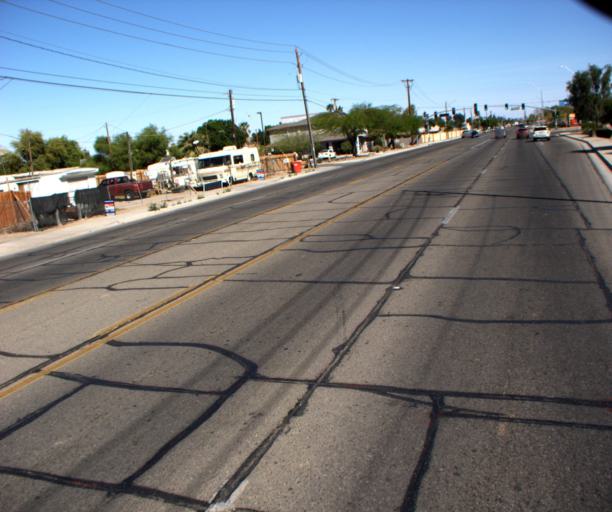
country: US
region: Arizona
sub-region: Yuma County
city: Yuma
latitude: 32.6791
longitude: -114.6502
